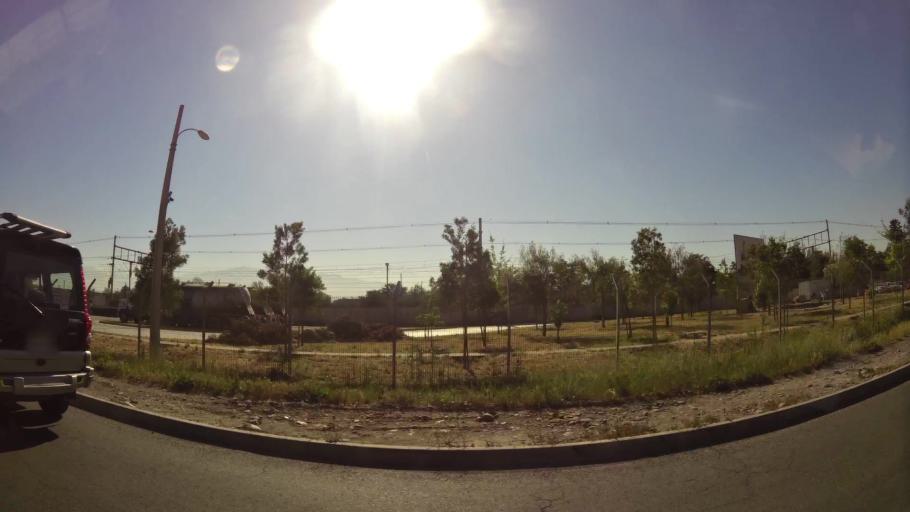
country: CL
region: Santiago Metropolitan
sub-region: Provincia de Maipo
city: San Bernardo
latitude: -33.5590
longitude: -70.6962
